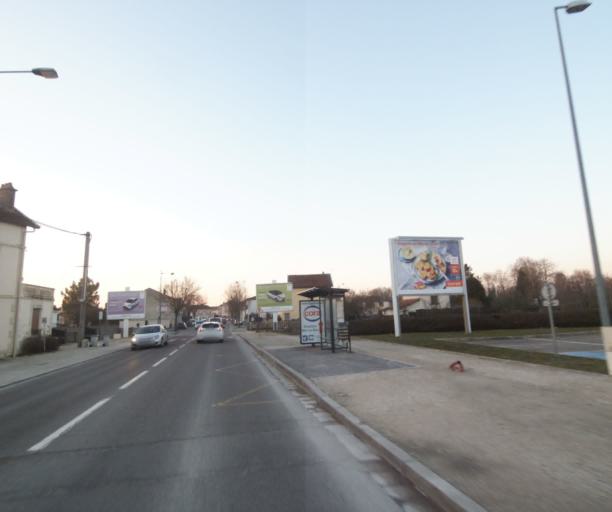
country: FR
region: Champagne-Ardenne
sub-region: Departement de la Haute-Marne
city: Saint-Dizier
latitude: 48.6287
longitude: 4.9574
